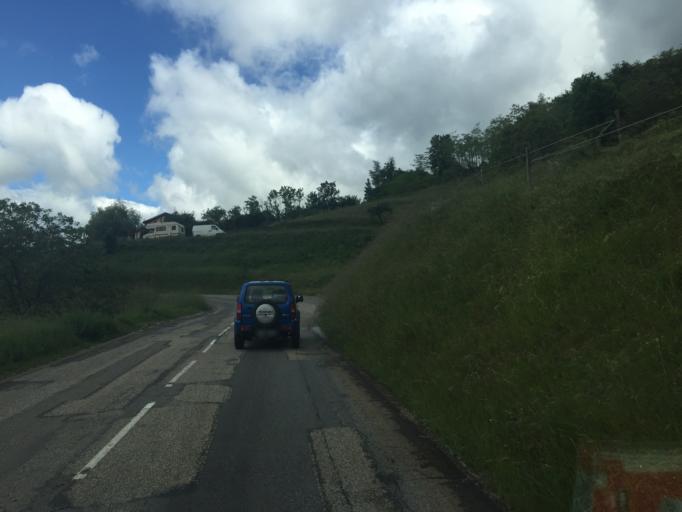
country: FR
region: Rhone-Alpes
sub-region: Departement de la Savoie
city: Barby
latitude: 45.5841
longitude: 6.0392
